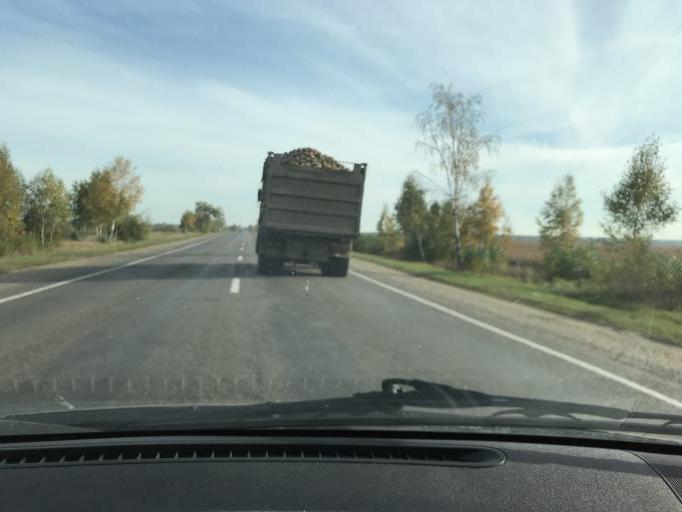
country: BY
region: Brest
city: Asnyezhytsy
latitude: 52.2123
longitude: 26.0454
